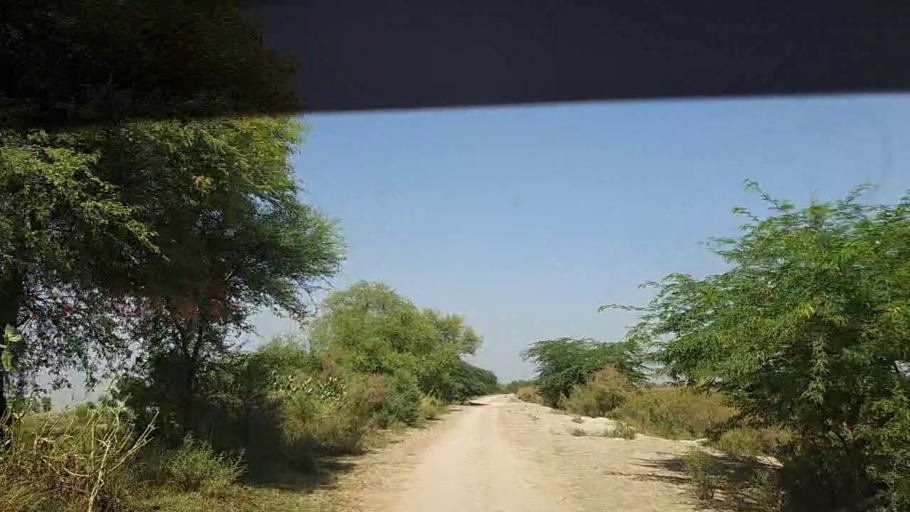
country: PK
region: Sindh
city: Ghauspur
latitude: 28.1741
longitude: 69.1466
